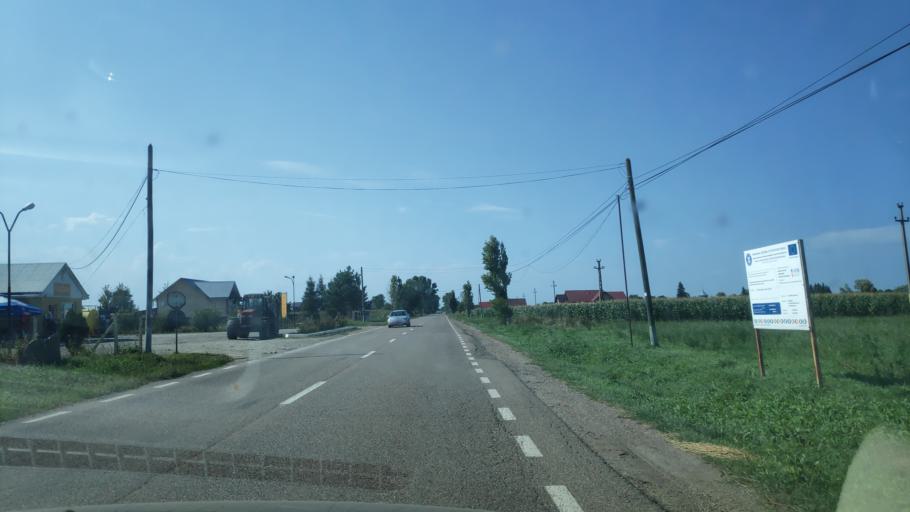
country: RO
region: Suceava
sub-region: Comuna Boroaia
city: Boroaia
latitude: 47.3721
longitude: 26.3274
